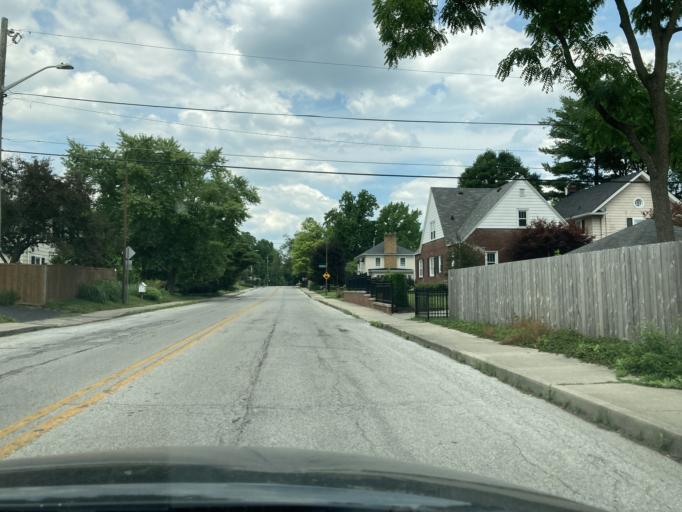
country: US
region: Indiana
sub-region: Marion County
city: Broad Ripple
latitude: 39.8351
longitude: -86.1616
